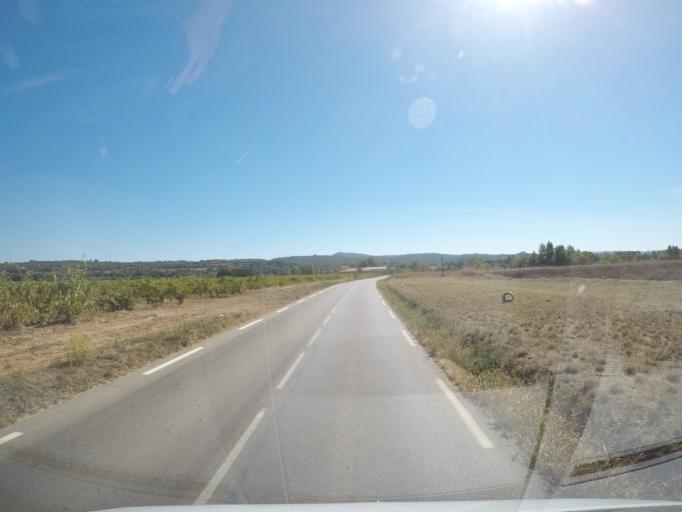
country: FR
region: Languedoc-Roussillon
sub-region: Departement de l'Herault
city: Aniane
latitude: 43.6983
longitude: 3.5758
